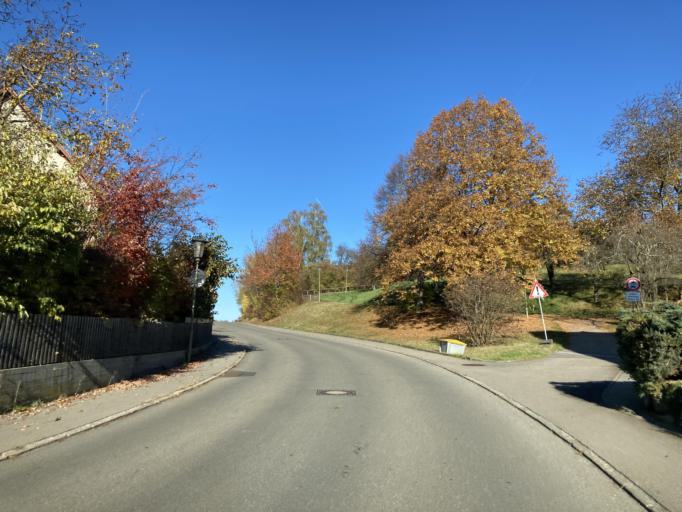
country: DE
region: Baden-Wuerttemberg
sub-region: Tuebingen Region
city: Mossingen
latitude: 48.3955
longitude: 9.0434
